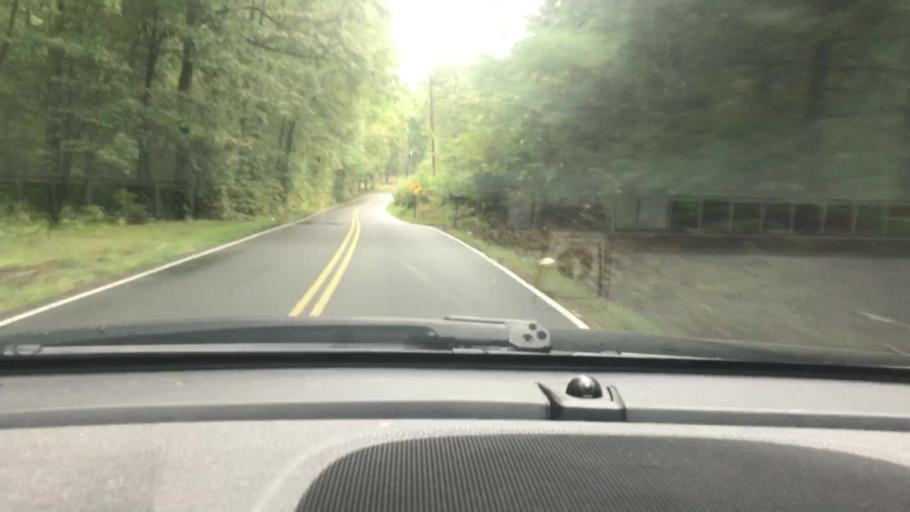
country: US
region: Tennessee
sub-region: Cheatham County
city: Kingston Springs
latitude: 36.1048
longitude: -87.1366
